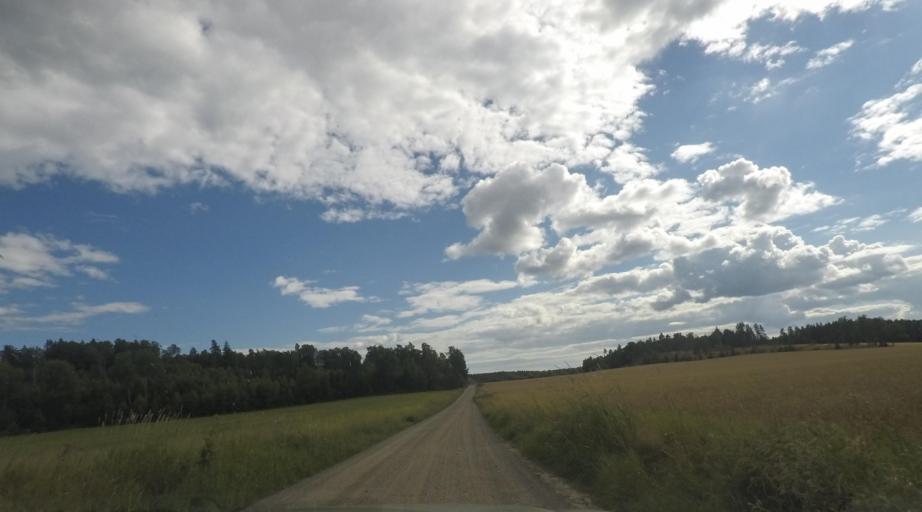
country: SE
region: Stockholm
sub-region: Sodertalje Kommun
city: Pershagen
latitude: 59.1193
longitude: 17.6568
